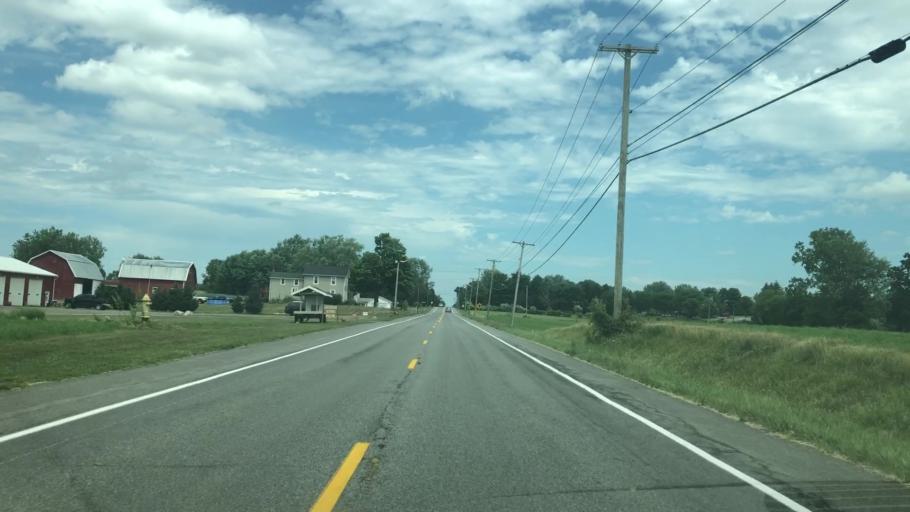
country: US
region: New York
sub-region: Monroe County
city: Fairport
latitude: 43.1502
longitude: -77.4006
